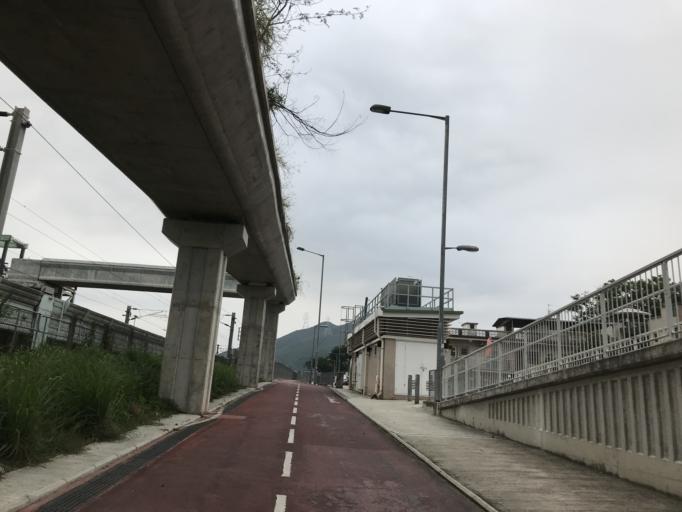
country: HK
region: Tai Po
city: Tai Po
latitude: 22.4711
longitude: 114.1536
